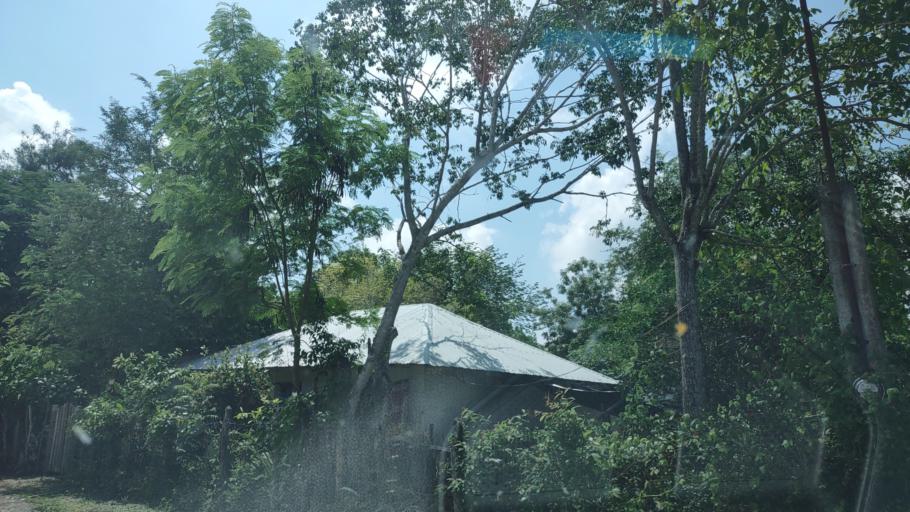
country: MX
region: Veracruz
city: Tempoal de Sanchez
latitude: 21.5469
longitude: -98.2768
